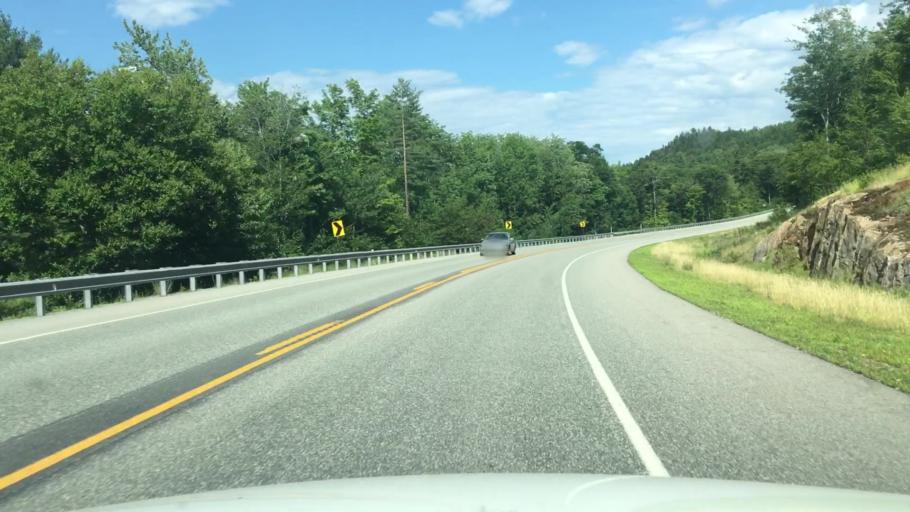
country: US
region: Maine
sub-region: Oxford County
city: Bethel
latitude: 44.3960
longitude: -70.9640
